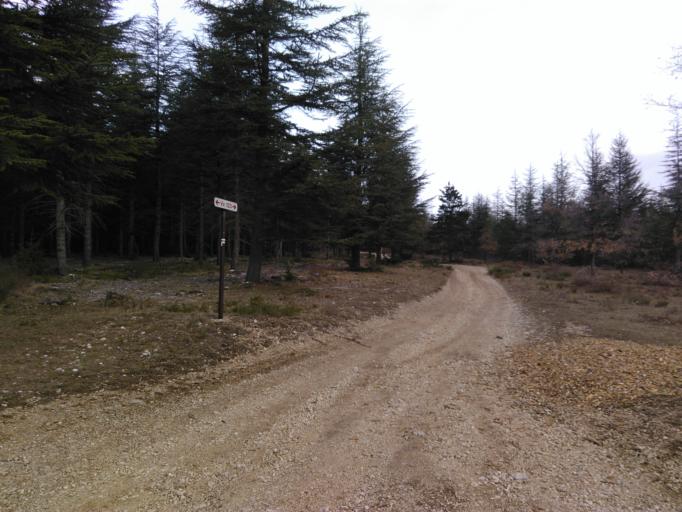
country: FR
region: Provence-Alpes-Cote d'Azur
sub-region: Departement du Vaucluse
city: Sault
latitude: 44.1194
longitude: 5.3506
